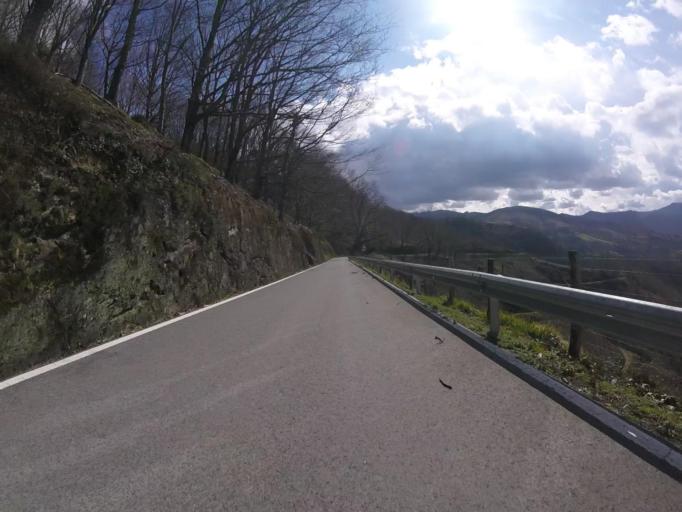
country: ES
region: Navarre
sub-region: Provincia de Navarra
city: Etxalar
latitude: 43.2557
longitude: -1.6187
